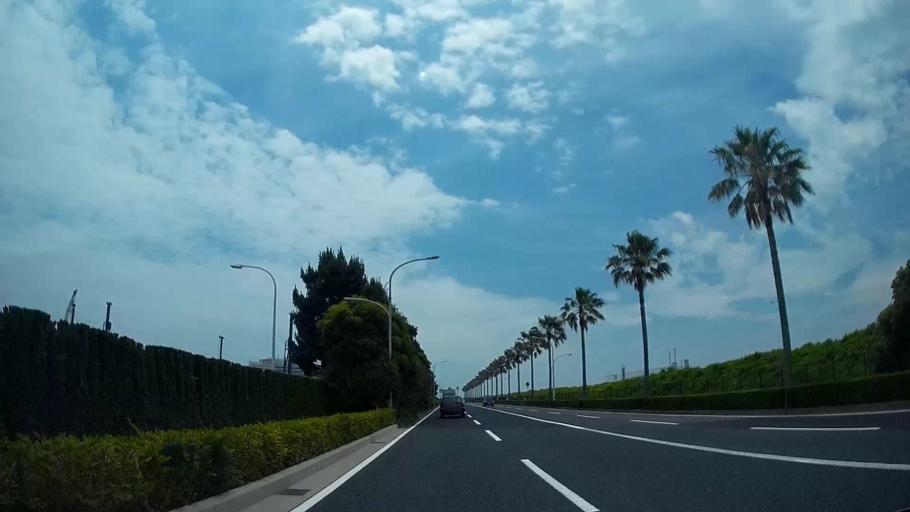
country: JP
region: Tokyo
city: Urayasu
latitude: 35.6363
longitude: 139.8749
